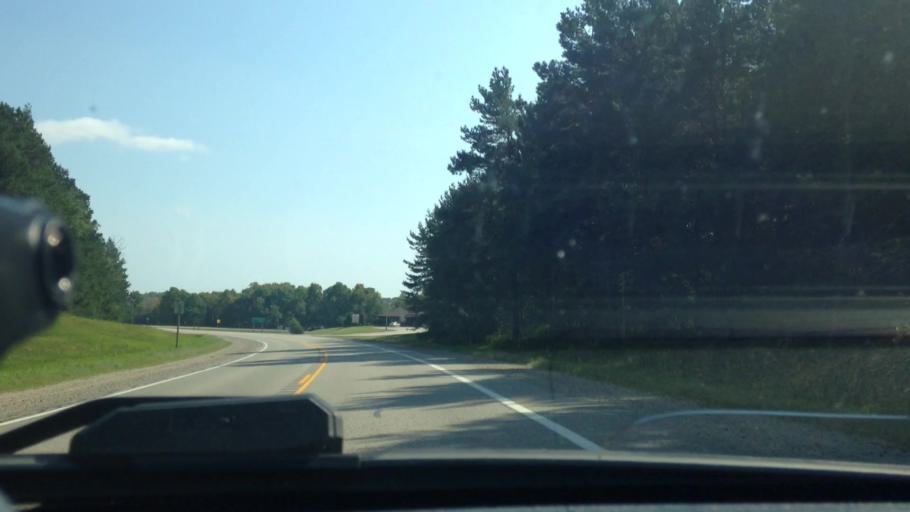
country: US
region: Michigan
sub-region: Luce County
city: Newberry
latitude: 46.3132
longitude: -85.6615
